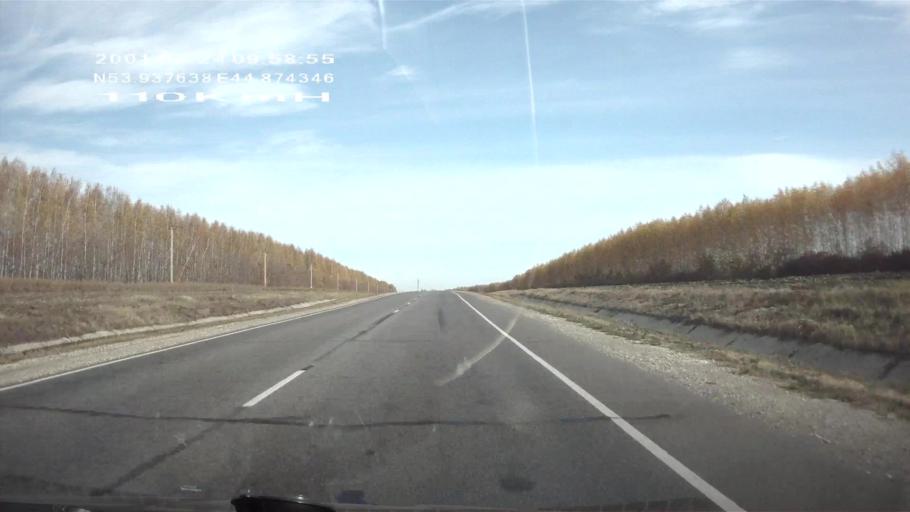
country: RU
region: Penza
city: Issa
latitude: 53.9382
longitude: 44.8749
